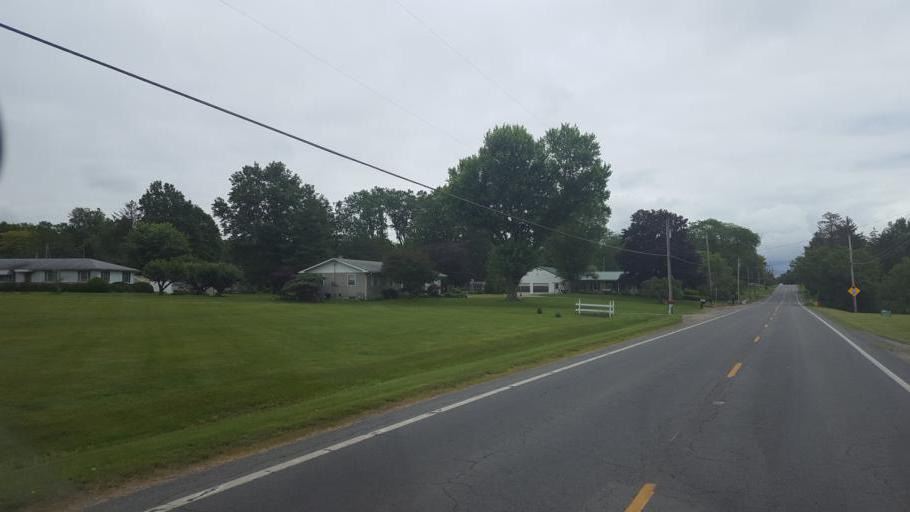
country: US
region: Ohio
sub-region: Crawford County
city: Galion
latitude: 40.7373
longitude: -82.8188
